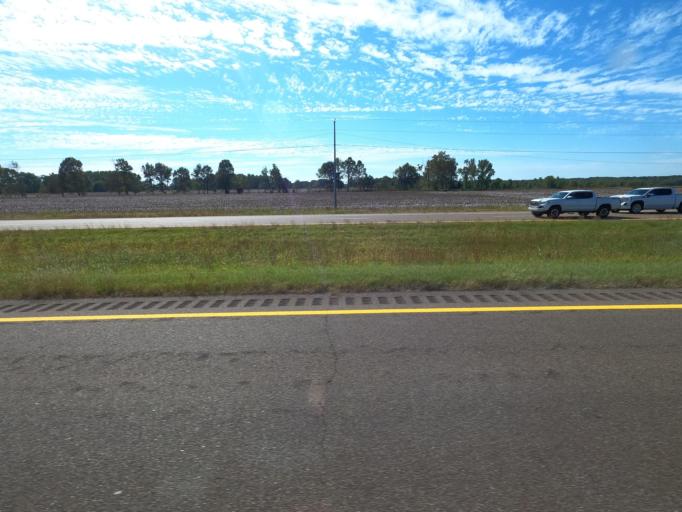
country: US
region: Tennessee
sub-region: Crockett County
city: Bells
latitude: 35.6958
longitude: -89.0099
